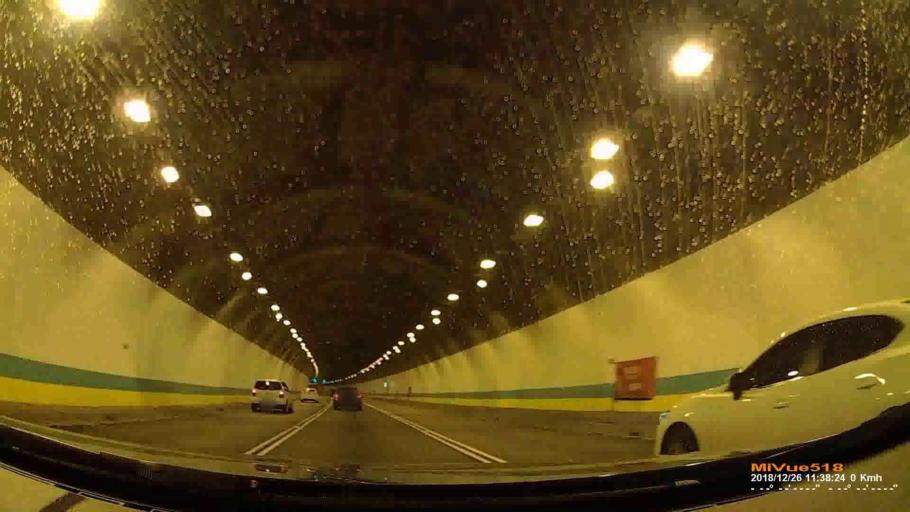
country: TW
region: Taipei
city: Taipei
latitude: 24.9799
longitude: 121.5842
